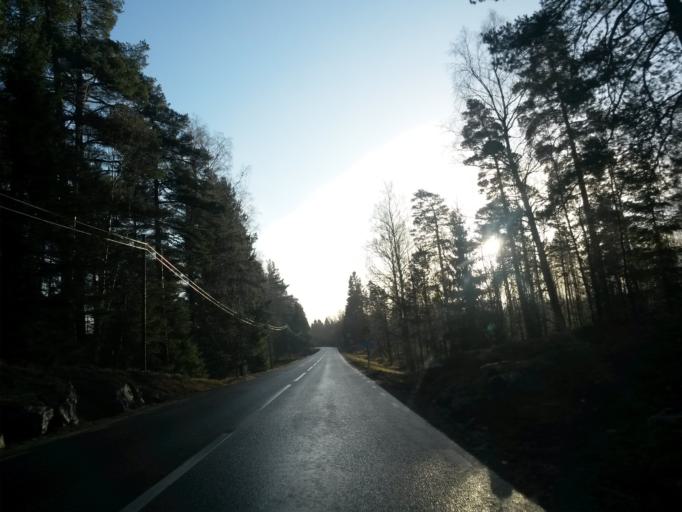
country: SE
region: Vaestra Goetaland
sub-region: Vargarda Kommun
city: Vargarda
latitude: 57.9078
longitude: 12.9064
